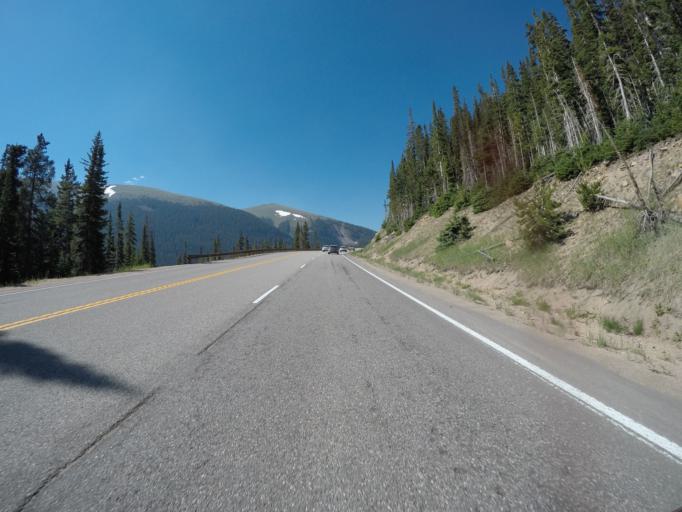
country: US
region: Colorado
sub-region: Clear Creek County
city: Georgetown
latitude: 39.8197
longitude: -105.7688
